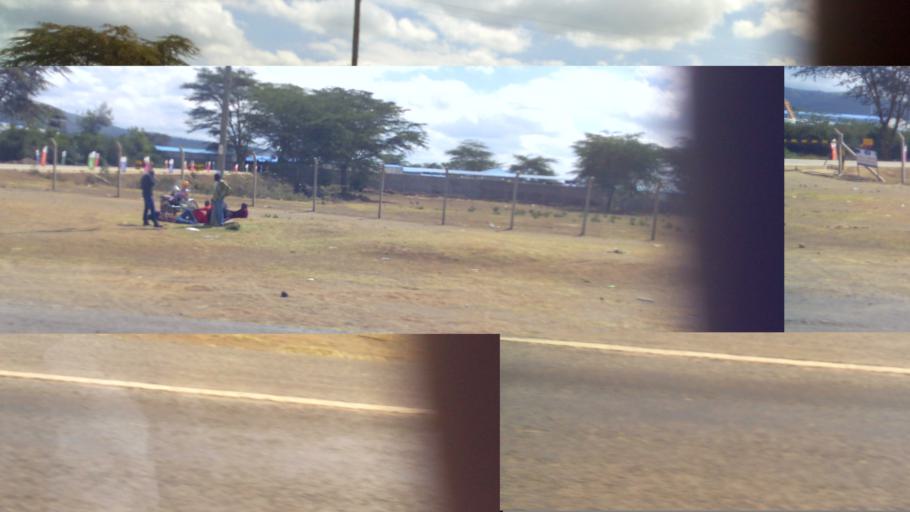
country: KE
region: Narok
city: Narok
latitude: -1.1045
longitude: 36.2224
